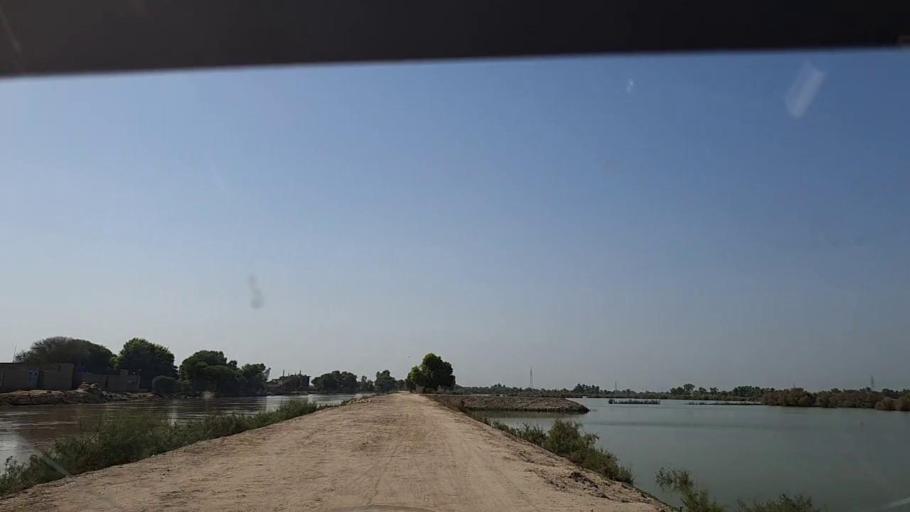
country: PK
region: Sindh
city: Ghauspur
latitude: 28.1790
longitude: 69.0900
